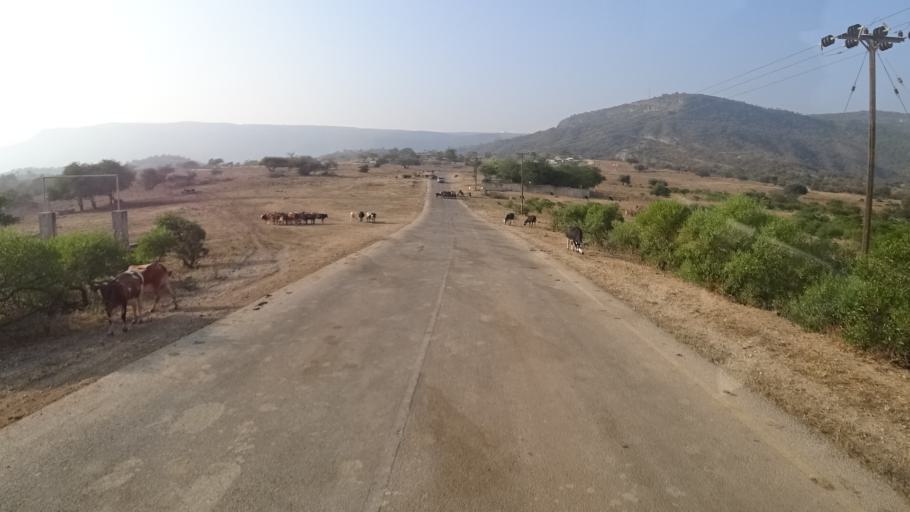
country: YE
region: Al Mahrah
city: Hawf
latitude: 16.7507
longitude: 53.3425
